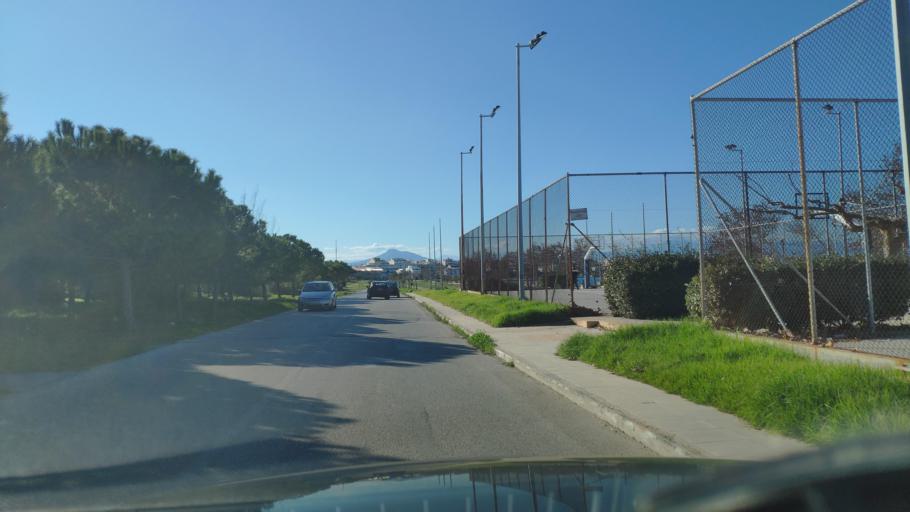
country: GR
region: Peloponnese
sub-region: Nomos Korinthias
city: Korinthos
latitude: 37.9421
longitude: 22.9456
